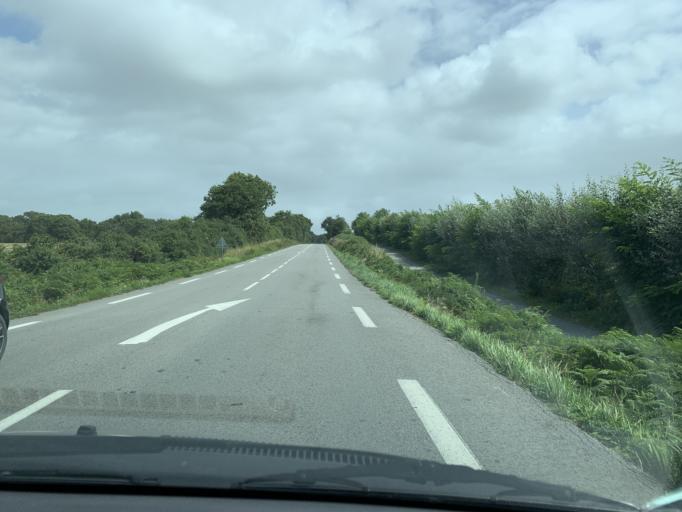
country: FR
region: Brittany
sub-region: Departement du Morbihan
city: Penestin
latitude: 47.4803
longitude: -2.4588
